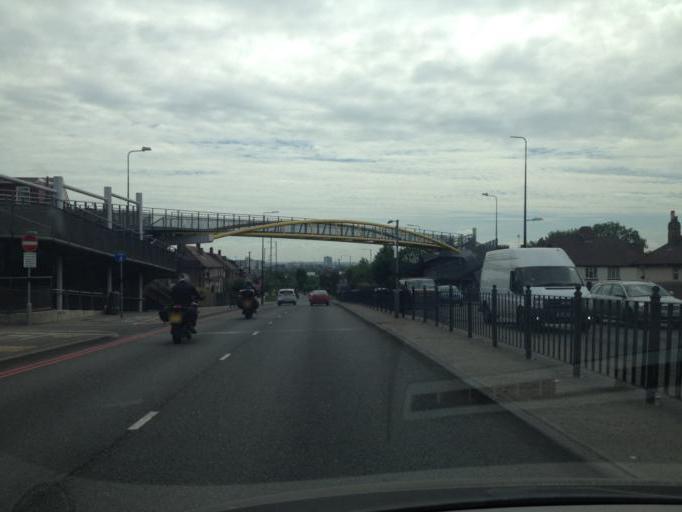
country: GB
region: England
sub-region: Greater London
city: Acton
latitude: 51.5161
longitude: -0.2590
